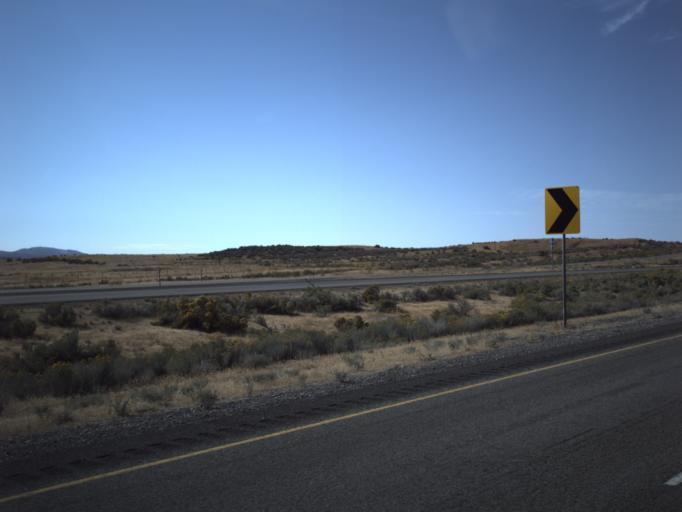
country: US
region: Utah
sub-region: Tooele County
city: Grantsville
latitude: 40.7716
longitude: -112.9800
